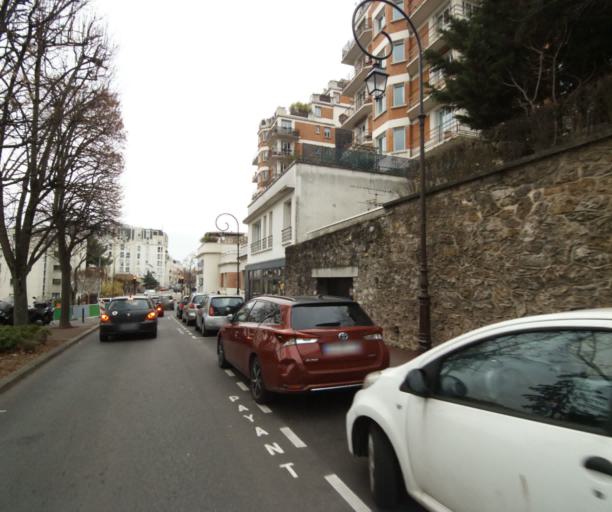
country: FR
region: Ile-de-France
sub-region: Departement des Hauts-de-Seine
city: Saint-Cloud
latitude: 48.8466
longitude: 2.2186
